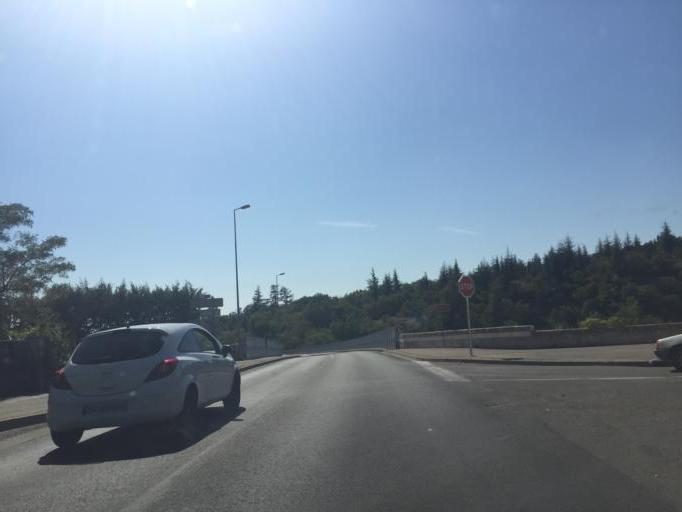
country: FR
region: Provence-Alpes-Cote d'Azur
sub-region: Departement des Alpes-de-Haute-Provence
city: Forcalquier
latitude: 43.9551
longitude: 5.7742
